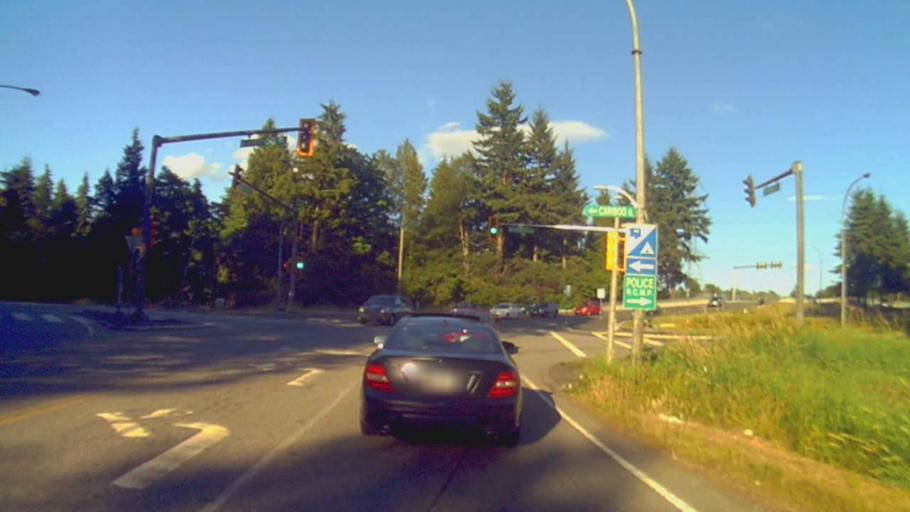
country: CA
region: British Columbia
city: New Westminster
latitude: 49.2458
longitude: -122.9122
